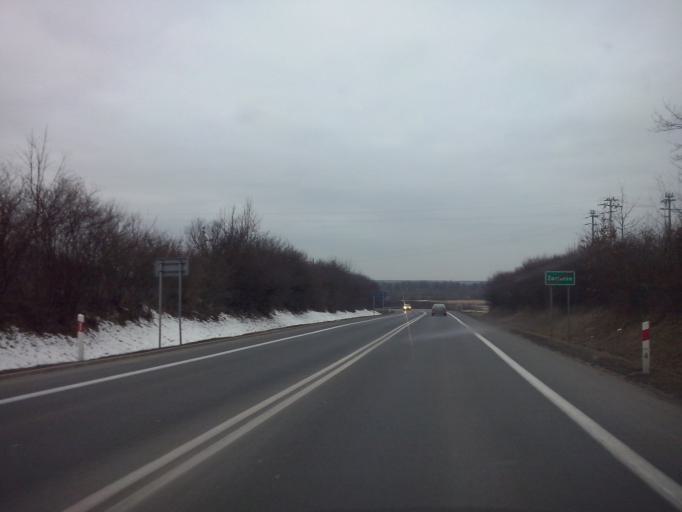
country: PL
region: Subcarpathian Voivodeship
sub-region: Powiat nizanski
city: Zarzecze
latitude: 50.5268
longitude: 22.1936
